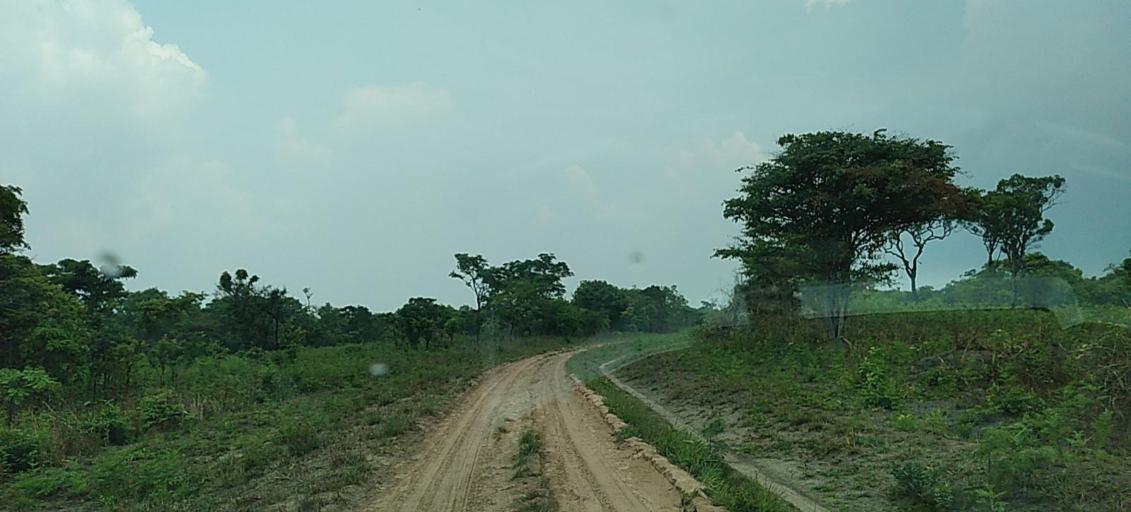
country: ZM
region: North-Western
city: Mwinilunga
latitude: -11.4307
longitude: 24.5926
